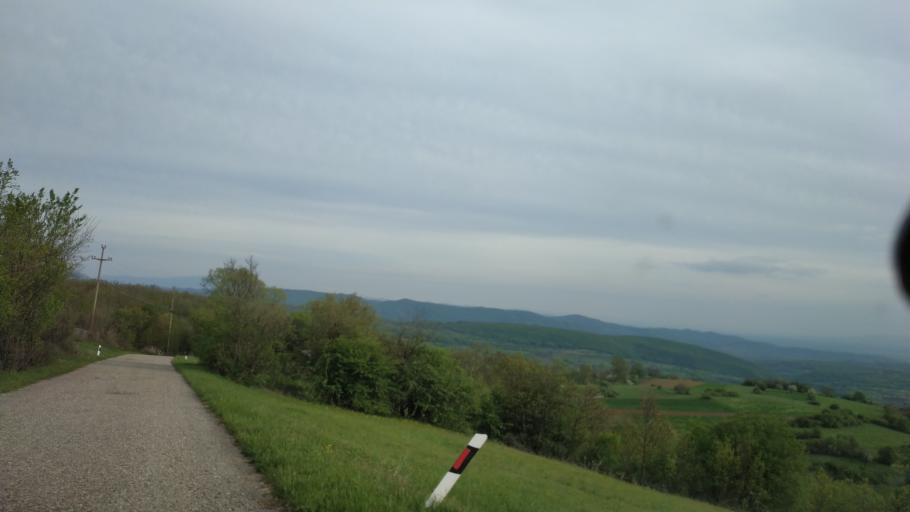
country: RS
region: Central Serbia
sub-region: Zajecarski Okrug
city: Soko Banja
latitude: 43.5410
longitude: 21.8792
